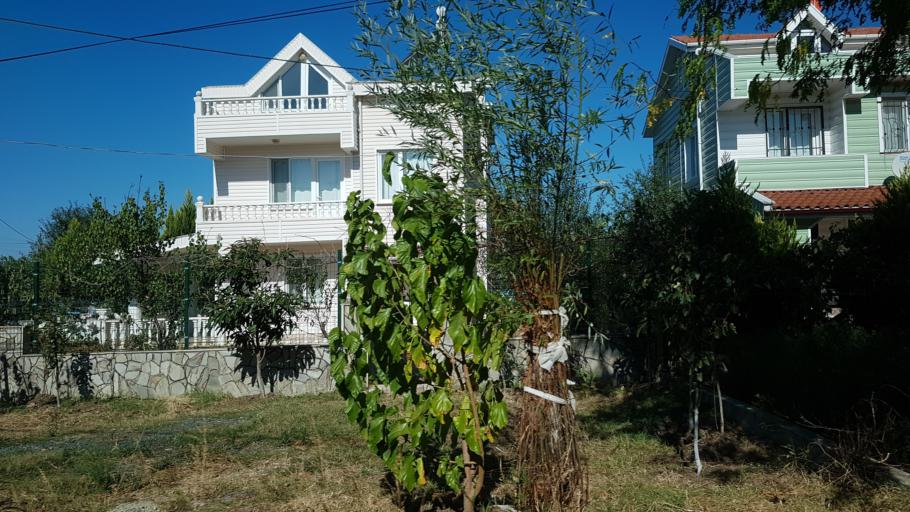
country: TR
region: Tekirdag
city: Corlu
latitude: 41.0090
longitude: 27.7979
